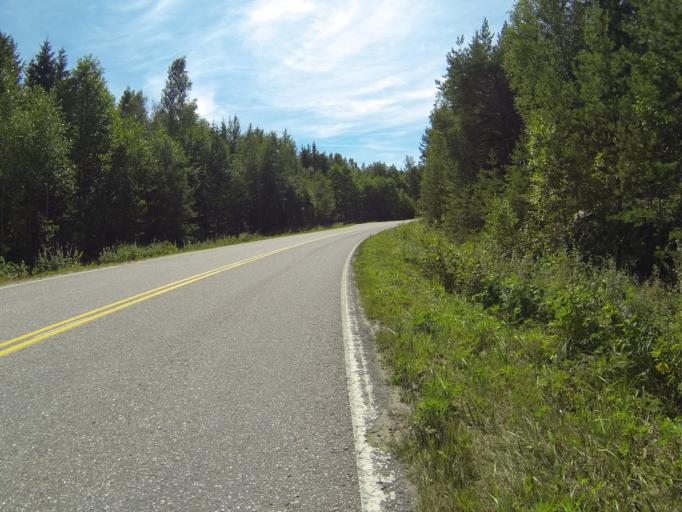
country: FI
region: Varsinais-Suomi
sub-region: Salo
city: Saerkisalo
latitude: 60.2649
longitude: 22.9739
